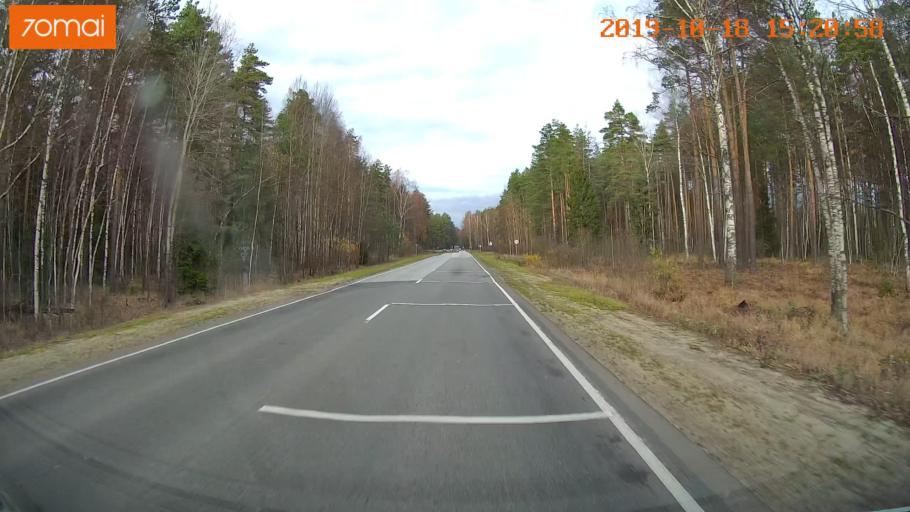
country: RU
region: Vladimir
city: Anopino
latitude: 55.6929
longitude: 40.7481
